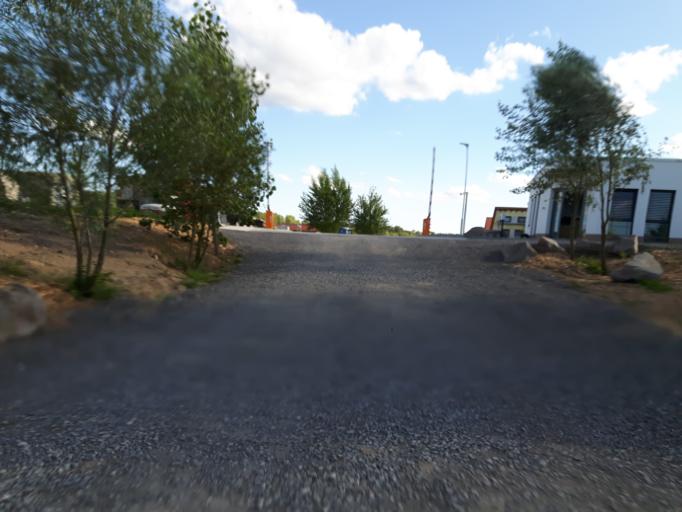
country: DE
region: Rheinland-Pfalz
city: Otterstadt
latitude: 49.3805
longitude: 8.4793
